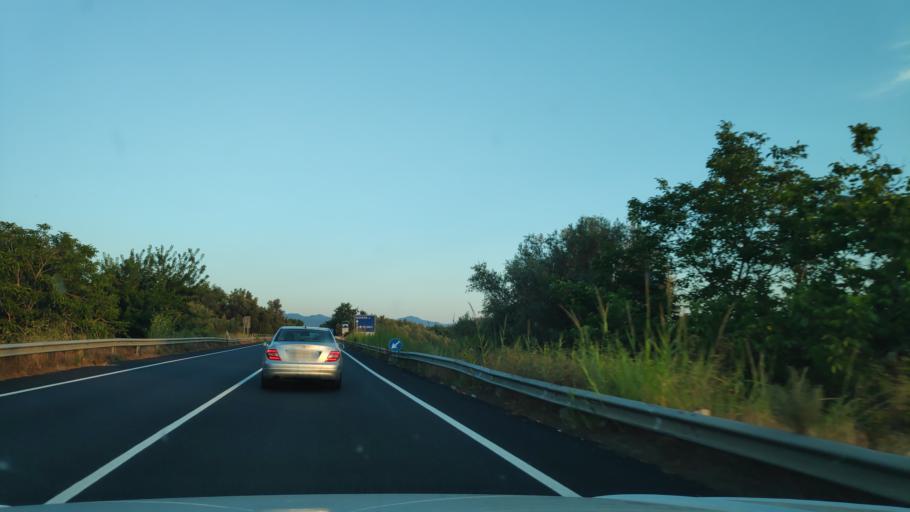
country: IT
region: Calabria
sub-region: Provincia di Reggio Calabria
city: Melicucco
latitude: 38.4366
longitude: 16.0472
